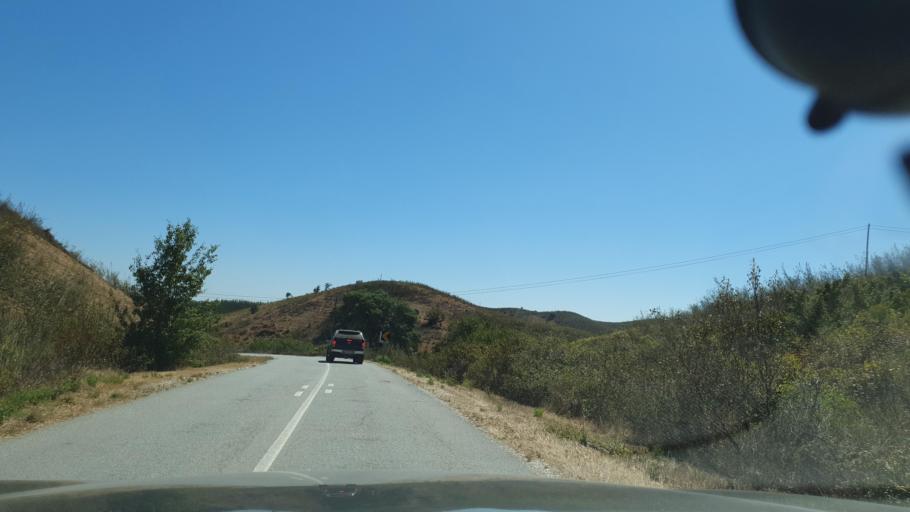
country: PT
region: Faro
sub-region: Monchique
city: Monchique
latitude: 37.4203
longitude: -8.5425
